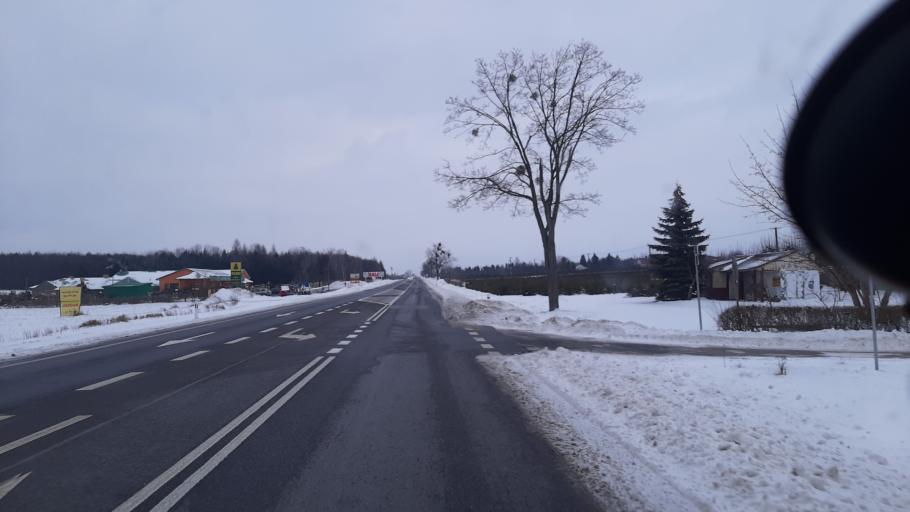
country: PL
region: Lublin Voivodeship
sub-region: Powiat pulawski
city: Kurow
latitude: 51.3859
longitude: 22.2082
